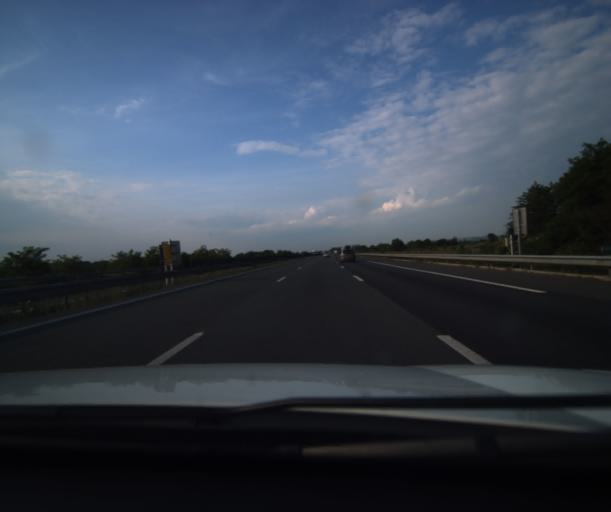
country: FR
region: Midi-Pyrenees
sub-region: Departement du Tarn-et-Garonne
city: Campsas
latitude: 43.9038
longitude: 1.3168
